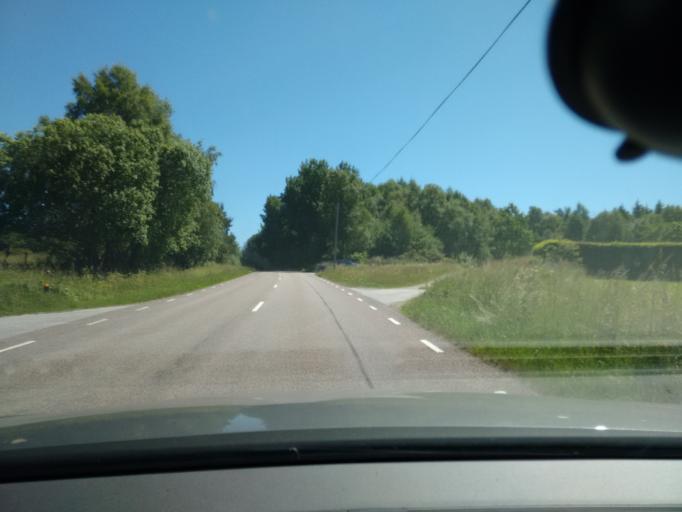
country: SE
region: Skane
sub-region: Horby Kommun
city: Hoerby
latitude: 55.7954
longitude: 13.8113
